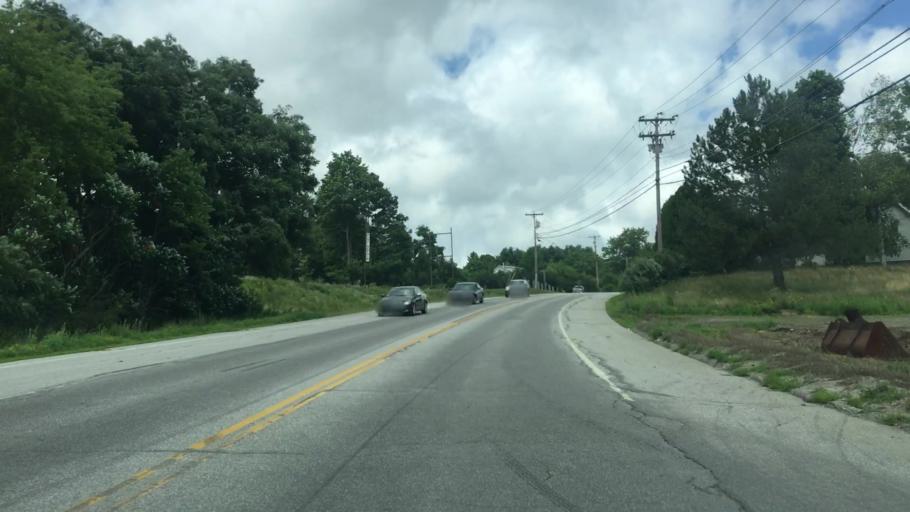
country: US
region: Maine
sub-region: Kennebec County
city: Hallowell
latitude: 44.2855
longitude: -69.7768
